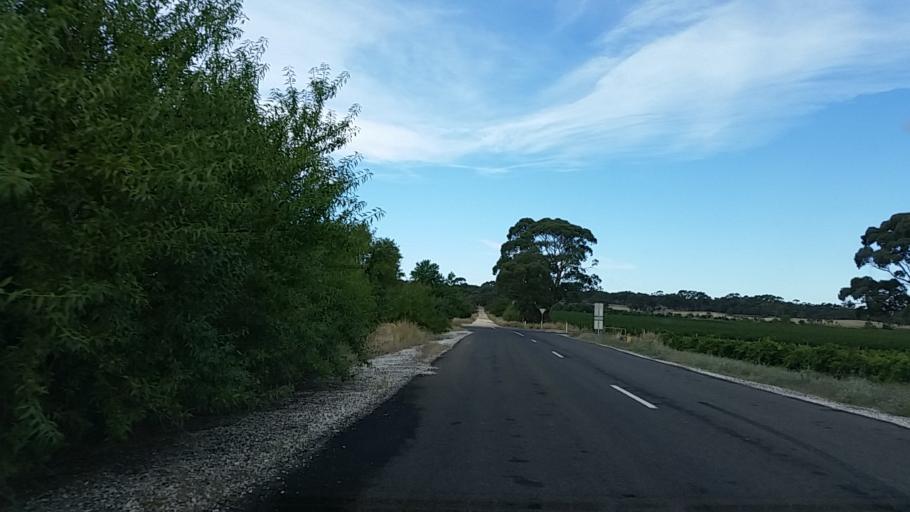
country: AU
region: South Australia
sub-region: Barossa
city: Nuriootpa
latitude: -34.4491
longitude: 139.0456
